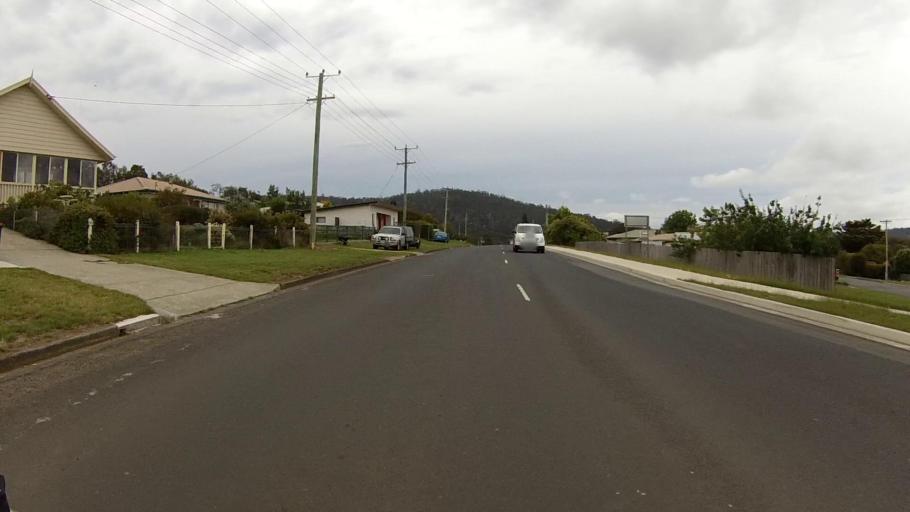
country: AU
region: Tasmania
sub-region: Sorell
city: Sorell
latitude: -42.5660
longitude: 147.8737
